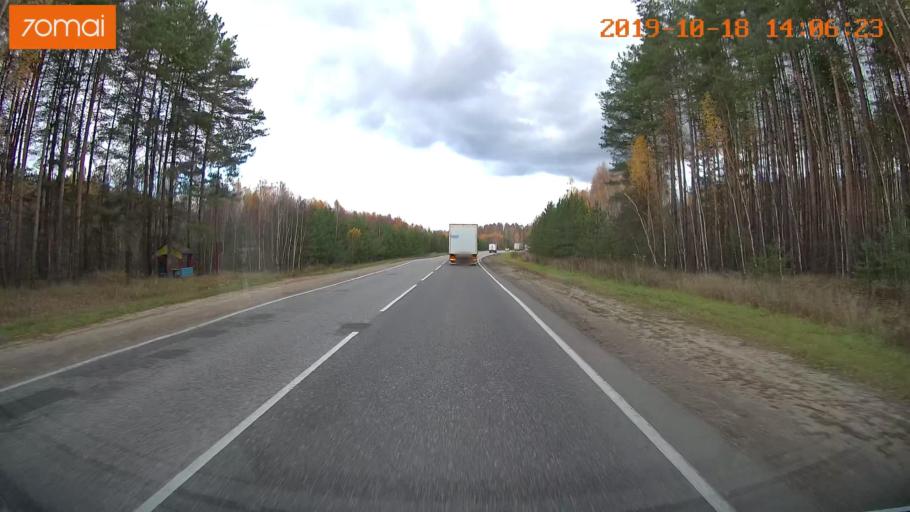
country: RU
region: Rjazan
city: Spas-Klepiki
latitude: 55.1447
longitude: 40.1499
